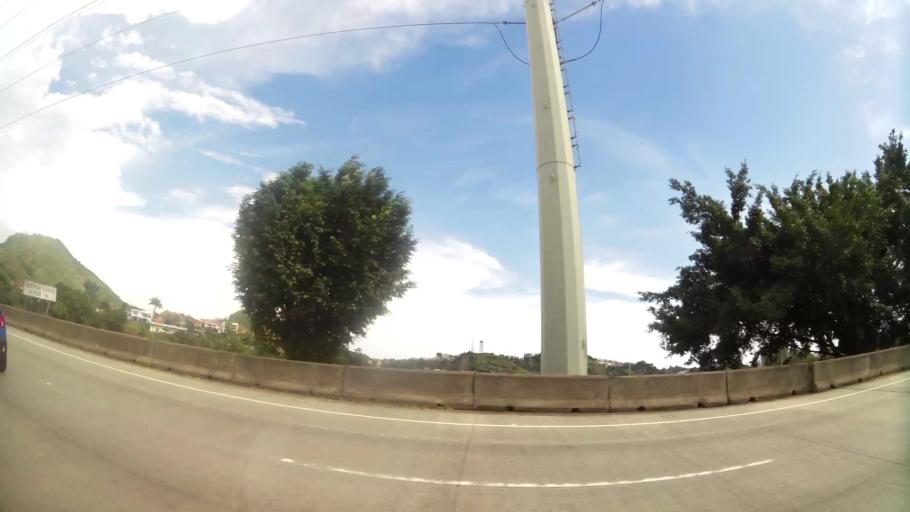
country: PA
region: Panama
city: Las Cumbres
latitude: 9.0432
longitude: -79.5295
